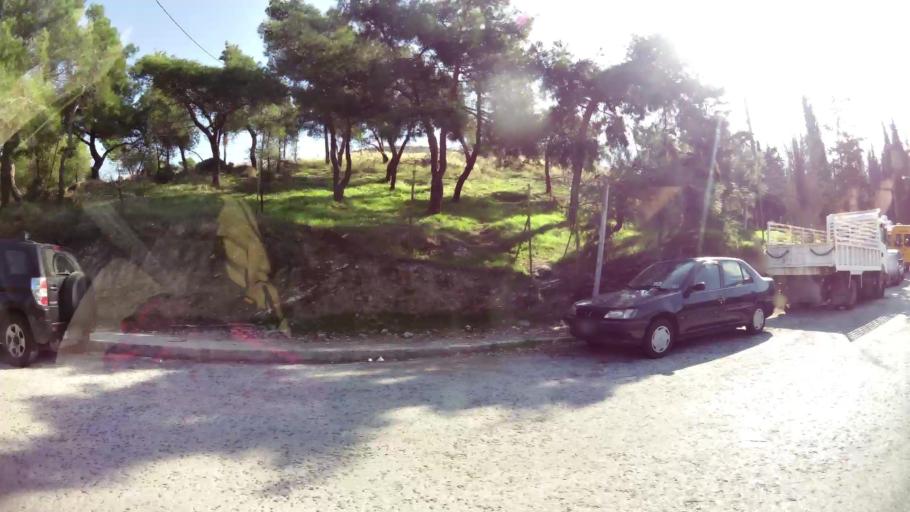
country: GR
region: Attica
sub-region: Nomarchia Athinas
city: Ilioupoli
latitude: 37.9452
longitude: 23.7734
